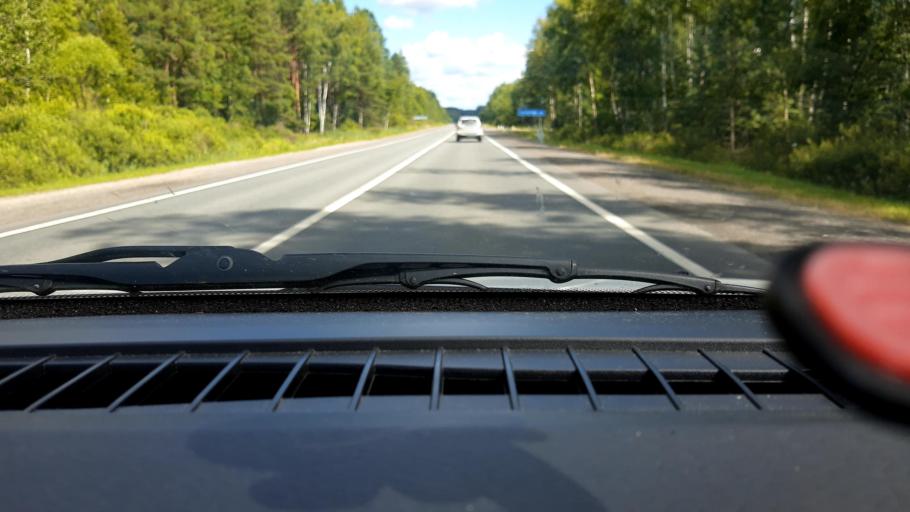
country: RU
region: Nizjnij Novgorod
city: Arzamas
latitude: 55.4867
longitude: 43.8876
